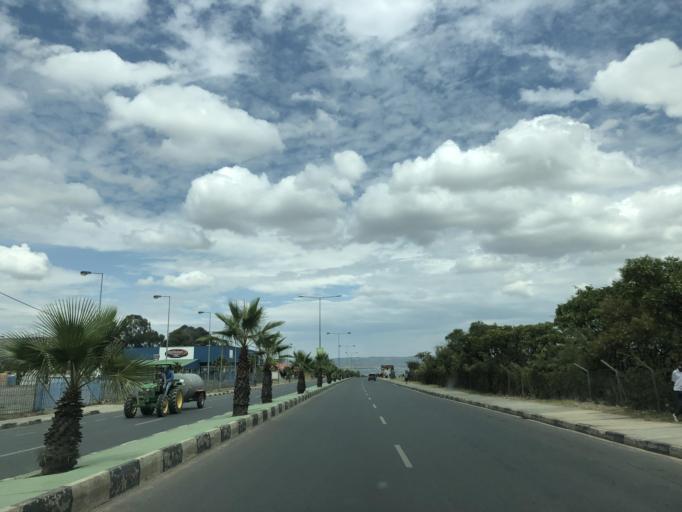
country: AO
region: Huila
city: Lubango
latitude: -14.9273
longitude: 13.5590
